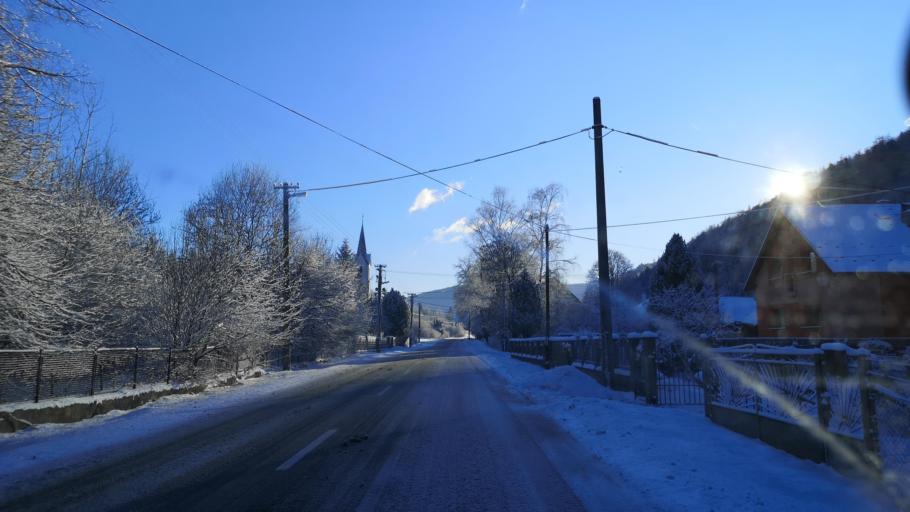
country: SK
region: Banskobystricky
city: Revuca
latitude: 48.8350
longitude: 20.0666
